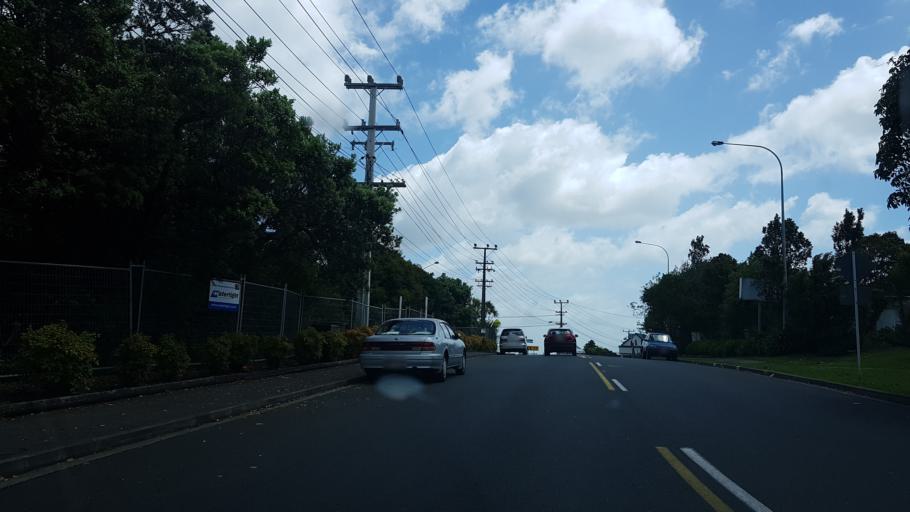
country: NZ
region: Auckland
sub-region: Auckland
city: North Shore
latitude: -36.8074
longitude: 174.7066
